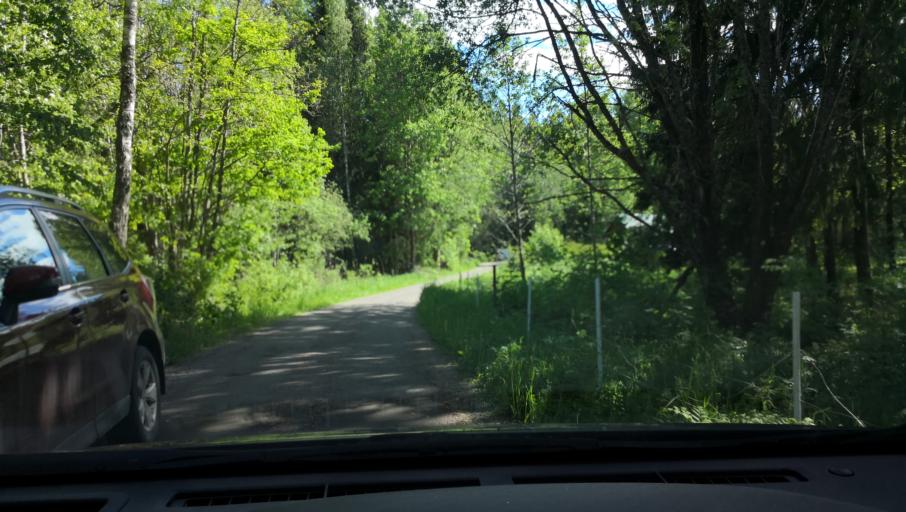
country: SE
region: Vaestmanland
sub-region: Arboga Kommun
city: Tyringe
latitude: 59.3214
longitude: 16.0017
